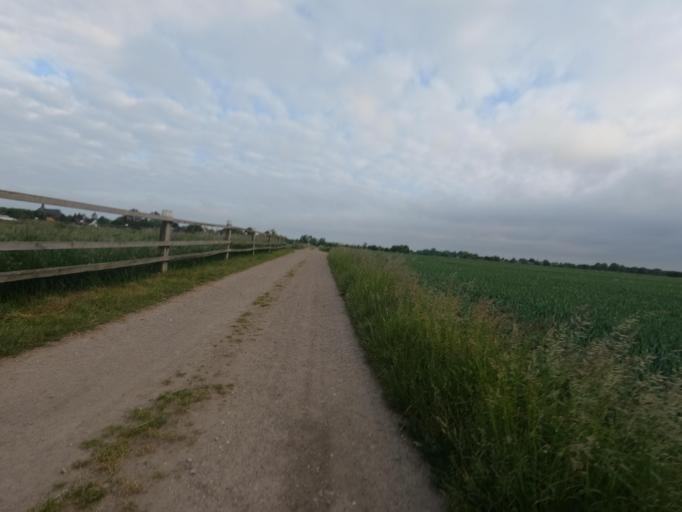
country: NL
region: Limburg
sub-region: Gemeente Roerdalen
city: Vlodrop
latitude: 51.1129
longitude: 6.1037
